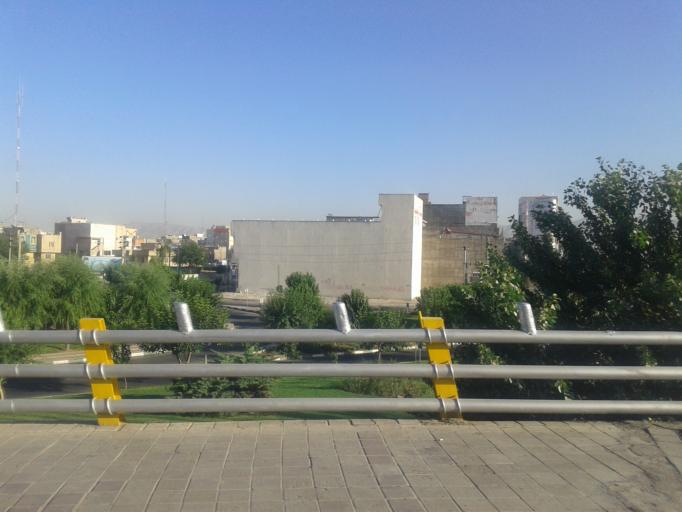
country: IR
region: Tehran
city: Rey
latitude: 35.6276
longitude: 51.3603
